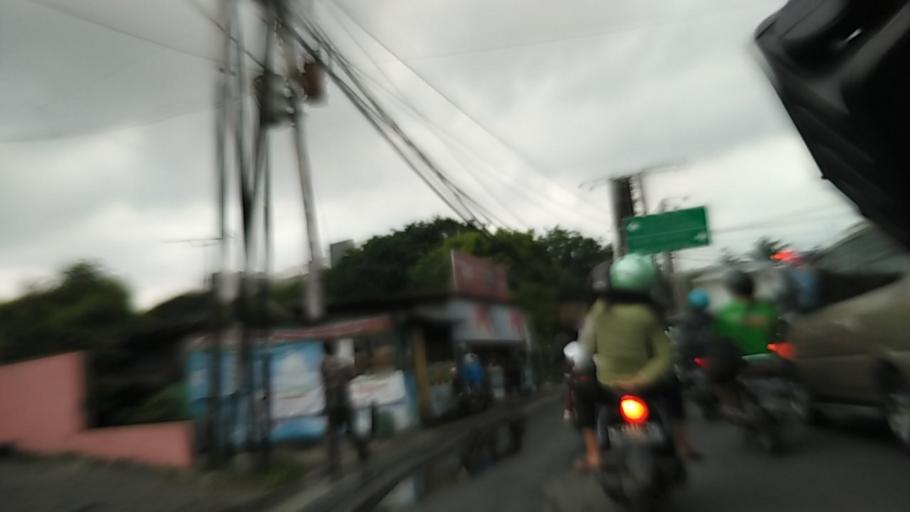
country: ID
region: Central Java
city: Semarang
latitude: -6.9947
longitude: 110.4061
